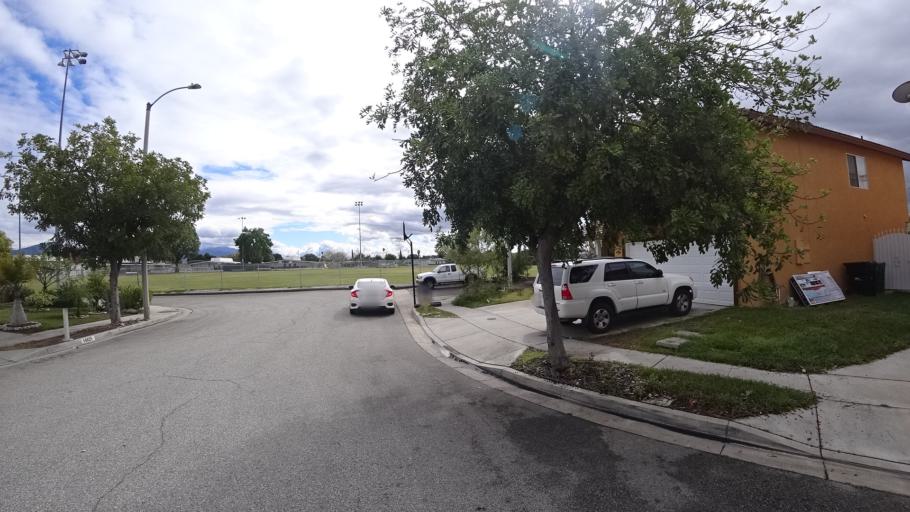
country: US
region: California
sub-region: Los Angeles County
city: Baldwin Park
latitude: 34.1019
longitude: -117.9543
